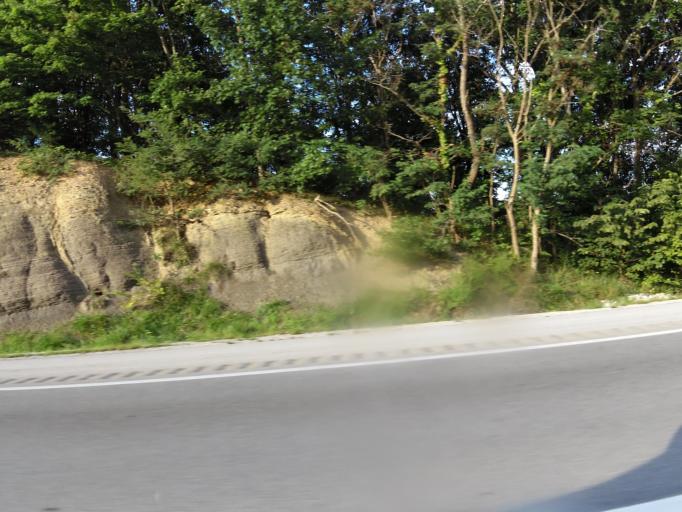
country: US
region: Kentucky
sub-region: Rockcastle County
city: Mount Vernon
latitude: 37.3041
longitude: -84.2838
